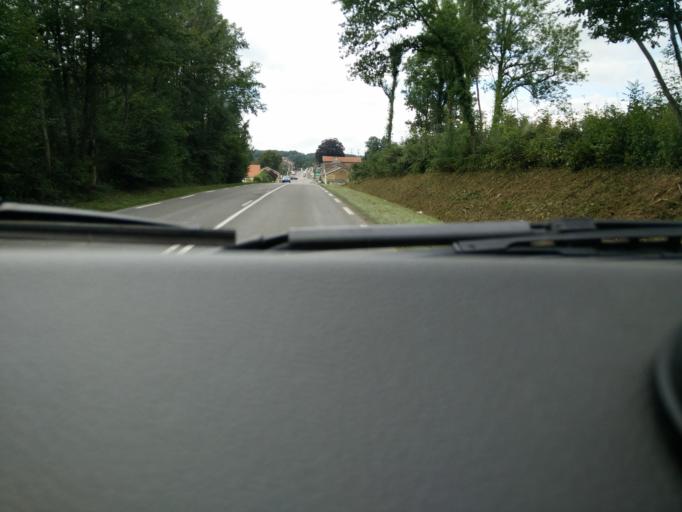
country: FR
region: Champagne-Ardenne
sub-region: Departement des Ardennes
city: Renwez
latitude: 49.8157
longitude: 4.5949
